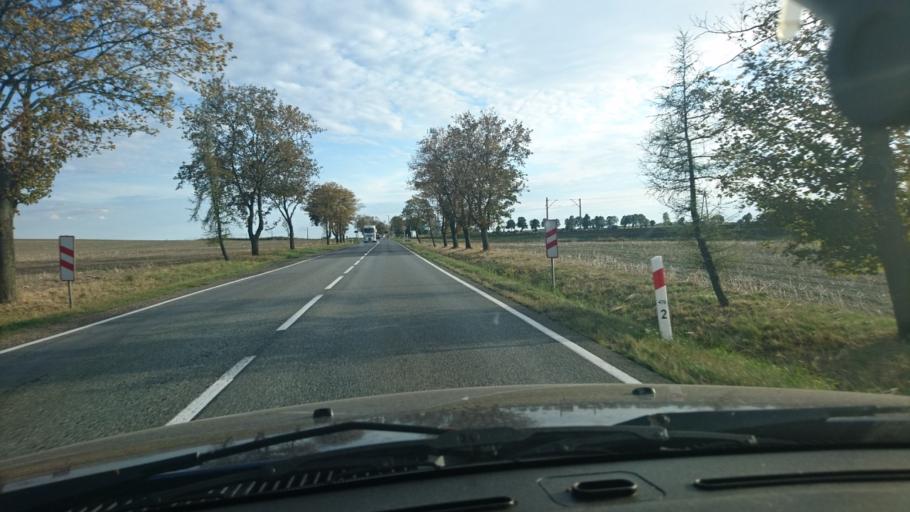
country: PL
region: Opole Voivodeship
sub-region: Powiat kluczborski
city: Byczyna
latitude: 51.1002
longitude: 18.2048
